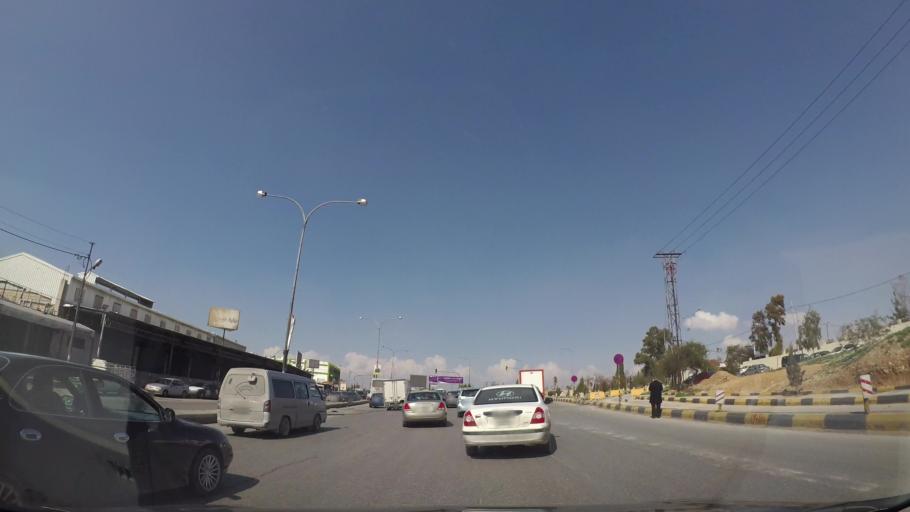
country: JO
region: Zarqa
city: Zarqa
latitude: 32.0551
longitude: 36.0948
